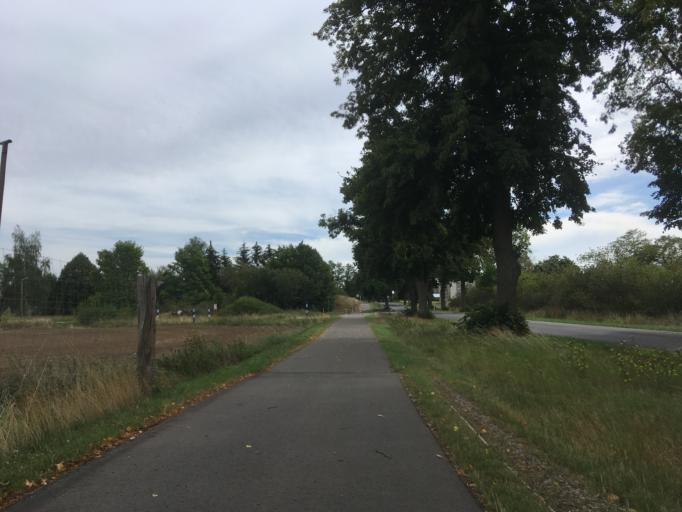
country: DE
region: Brandenburg
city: Mittenwalde
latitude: 53.2198
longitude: 13.6793
